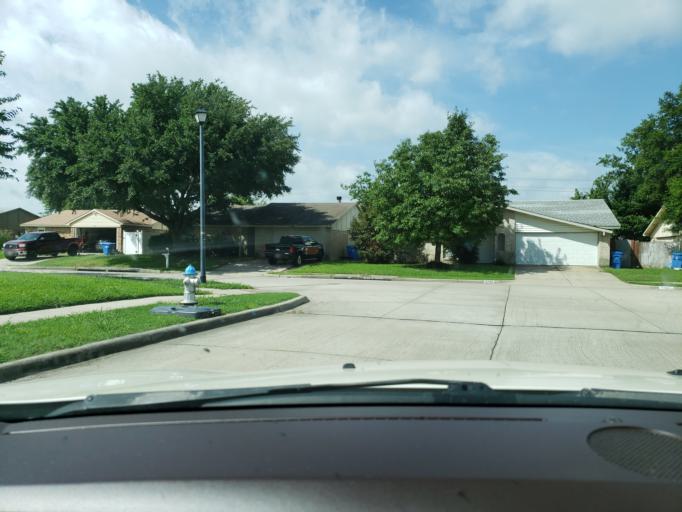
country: US
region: Texas
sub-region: Dallas County
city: Rowlett
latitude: 32.9129
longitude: -96.5748
